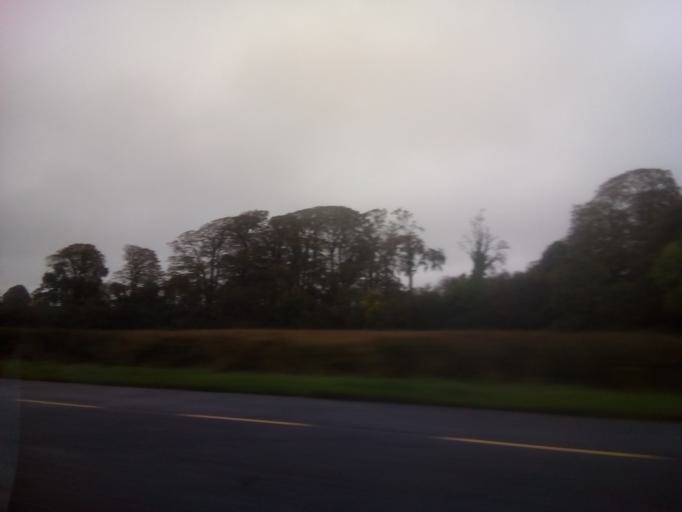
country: IE
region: Leinster
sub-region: An Iarmhi
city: An Muileann gCearr
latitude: 53.6041
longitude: -7.4124
